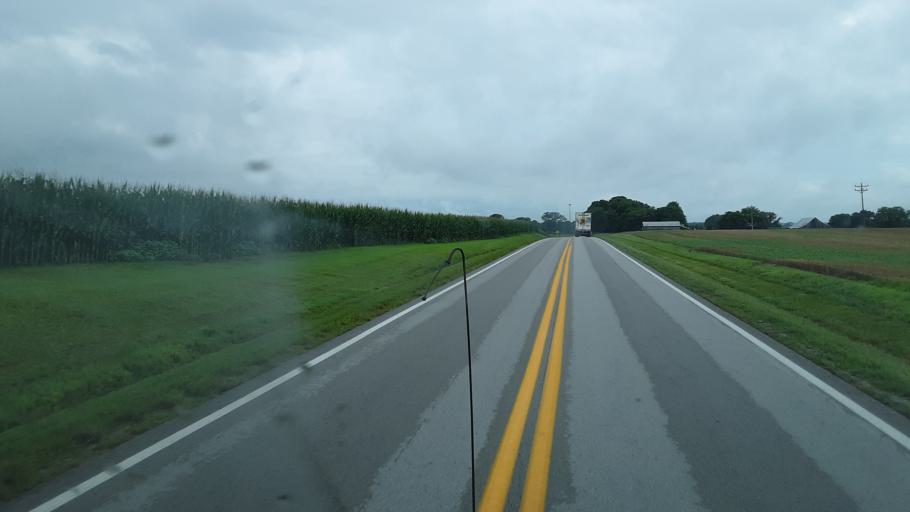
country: US
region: Kentucky
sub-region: Todd County
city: Elkton
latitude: 36.7510
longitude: -87.0434
